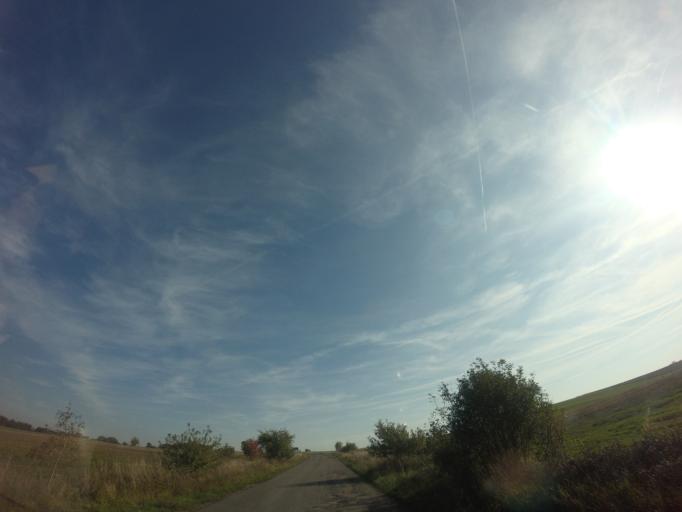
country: PL
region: West Pomeranian Voivodeship
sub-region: Powiat choszczenski
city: Recz
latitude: 53.2529
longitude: 15.5677
